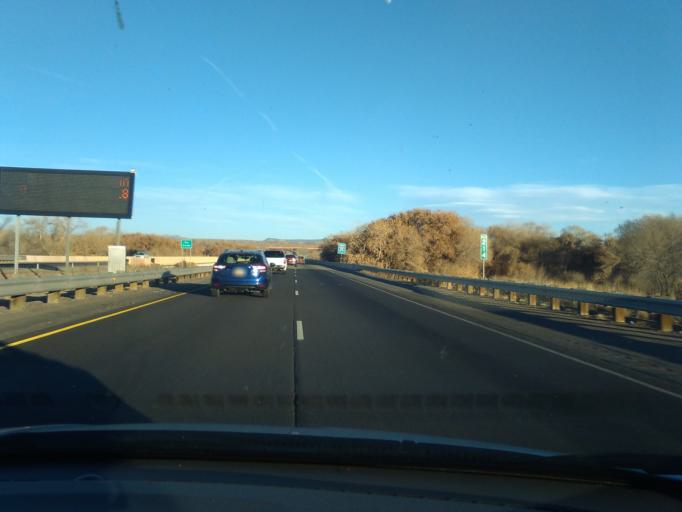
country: US
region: New Mexico
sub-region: Bernalillo County
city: South Valley
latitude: 34.9493
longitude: -106.6861
